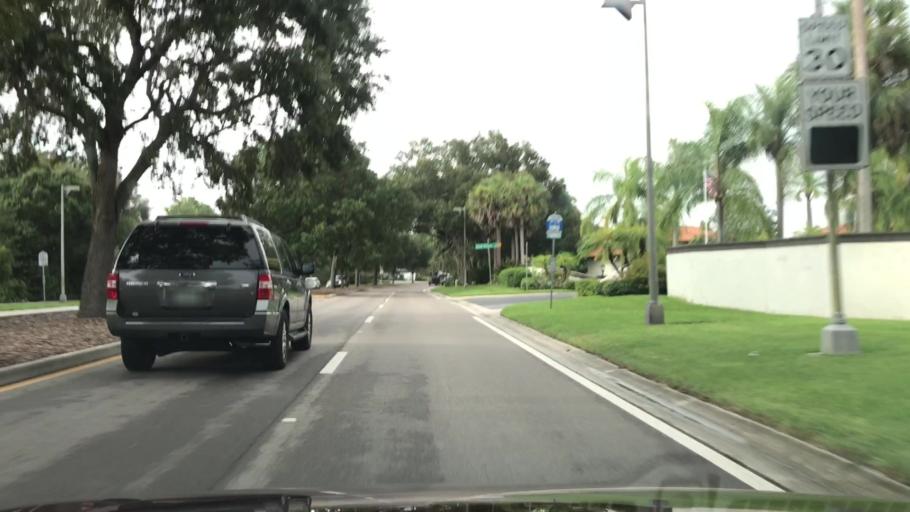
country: US
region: Florida
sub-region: Sarasota County
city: Venice Gardens
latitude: 27.0630
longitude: -82.3941
